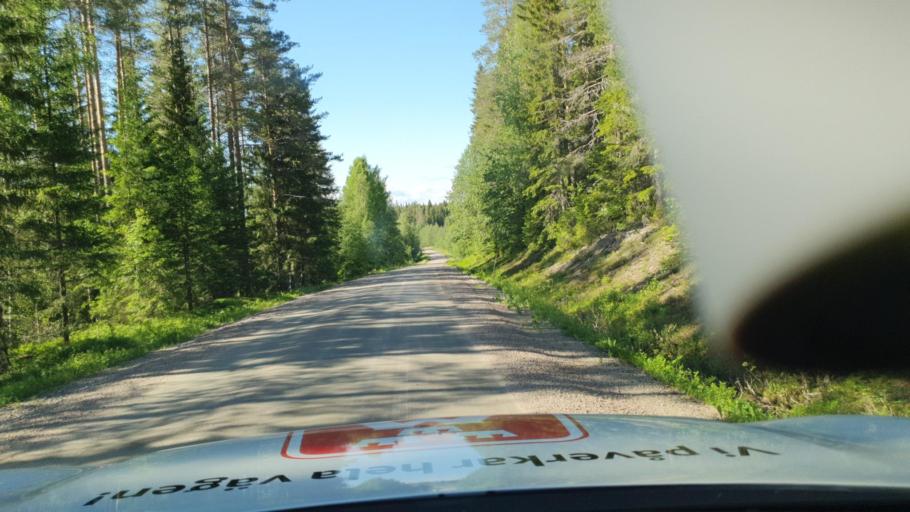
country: SE
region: Vaesterbotten
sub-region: Vannas Kommun
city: Vaennaes
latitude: 63.8399
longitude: 19.6289
